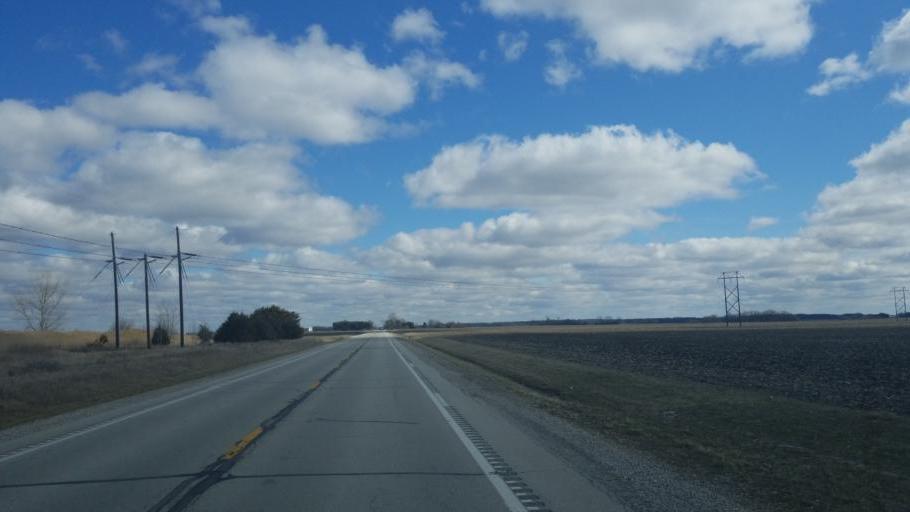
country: US
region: Illinois
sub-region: Douglas County
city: Villa Grove
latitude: 39.7921
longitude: -88.0492
